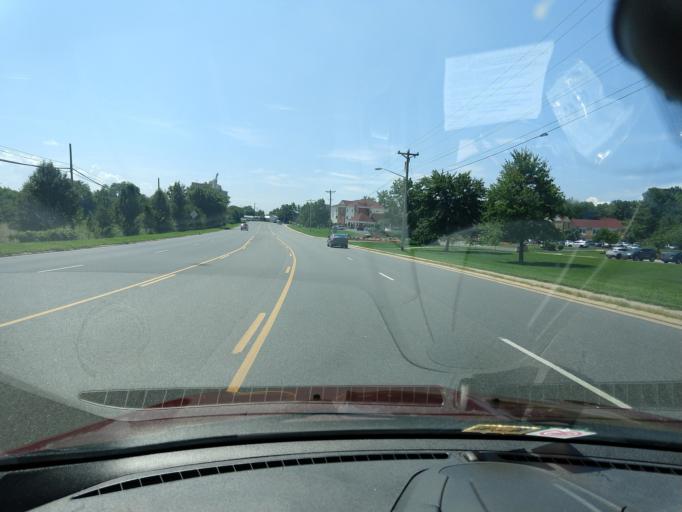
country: US
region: Virginia
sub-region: City of Harrisonburg
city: Harrisonburg
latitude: 38.4764
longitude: -78.8721
